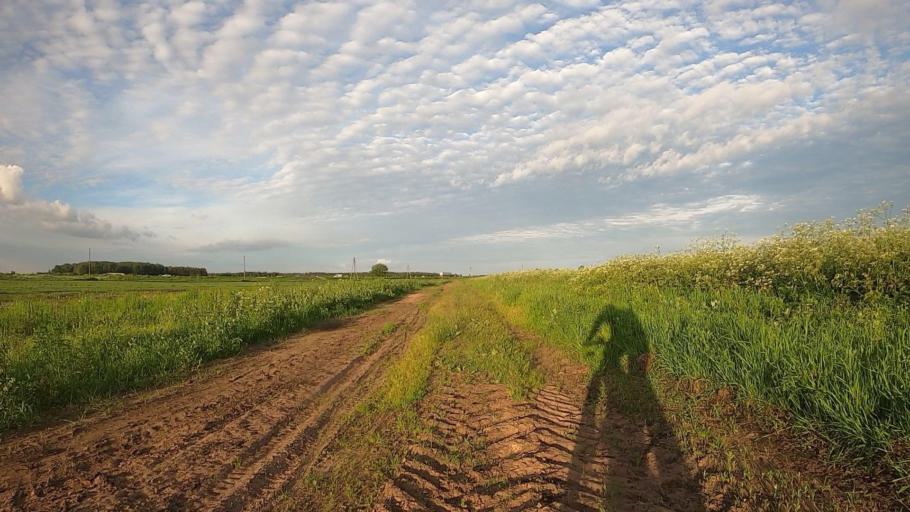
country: LV
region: Olaine
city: Olaine
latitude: 56.8662
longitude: 23.9680
